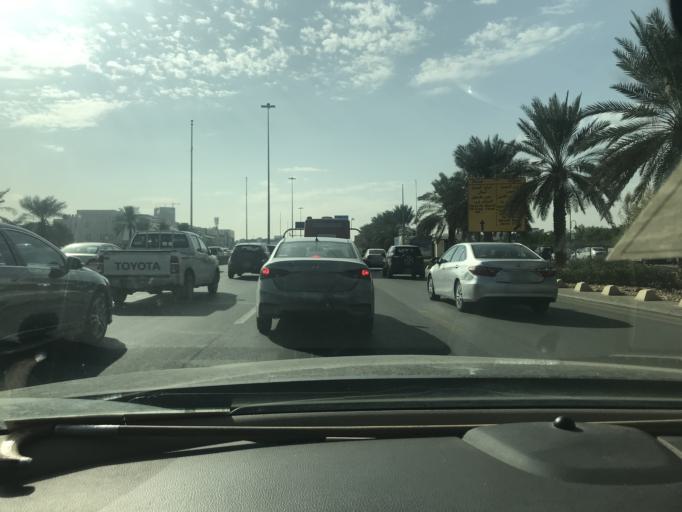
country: SA
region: Ar Riyad
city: Riyadh
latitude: 24.6853
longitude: 46.7038
